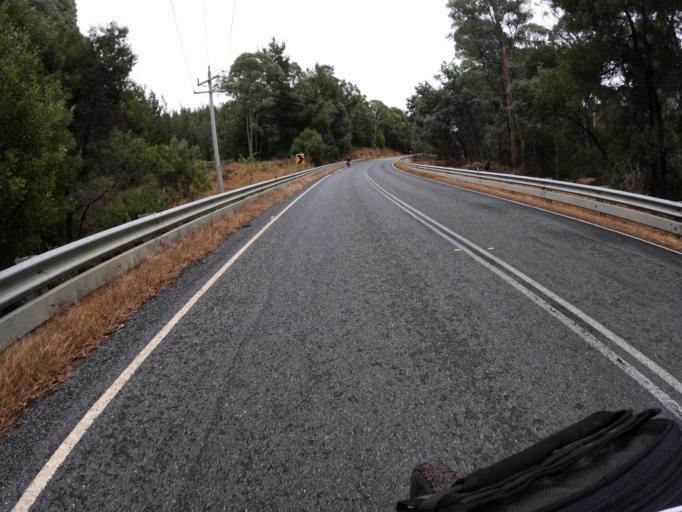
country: AU
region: New South Wales
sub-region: Greater Hume Shire
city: Holbrook
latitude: -36.1501
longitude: 147.4582
